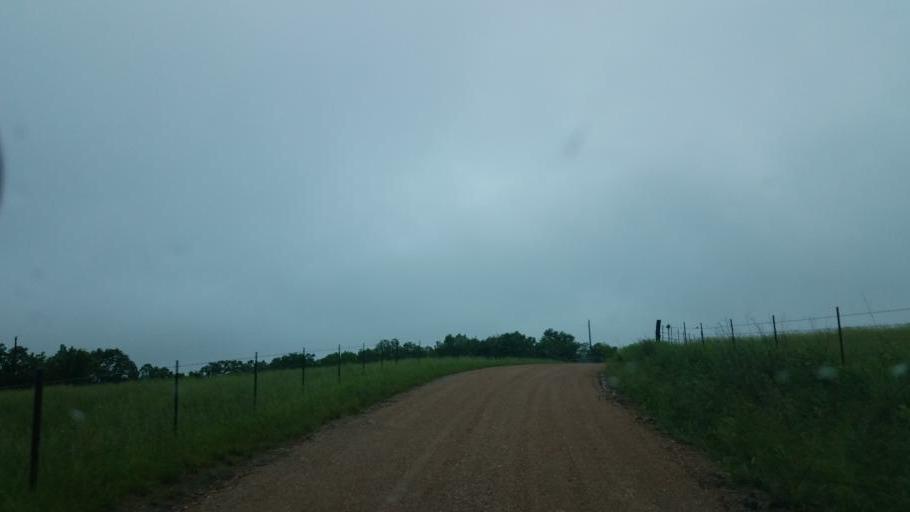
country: US
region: Missouri
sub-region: Moniteau County
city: California
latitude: 38.7167
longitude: -92.6006
